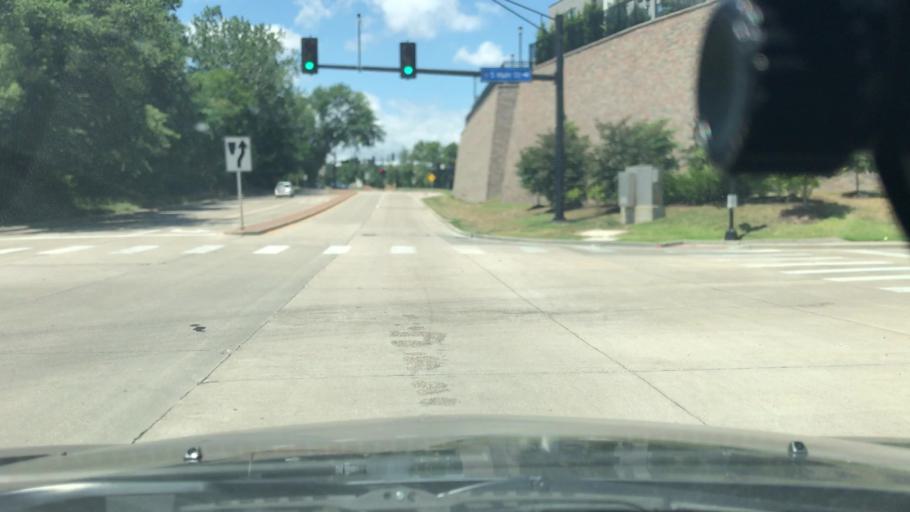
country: US
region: Missouri
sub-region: Saint Charles County
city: Saint Charles
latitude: 38.7638
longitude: -90.4946
